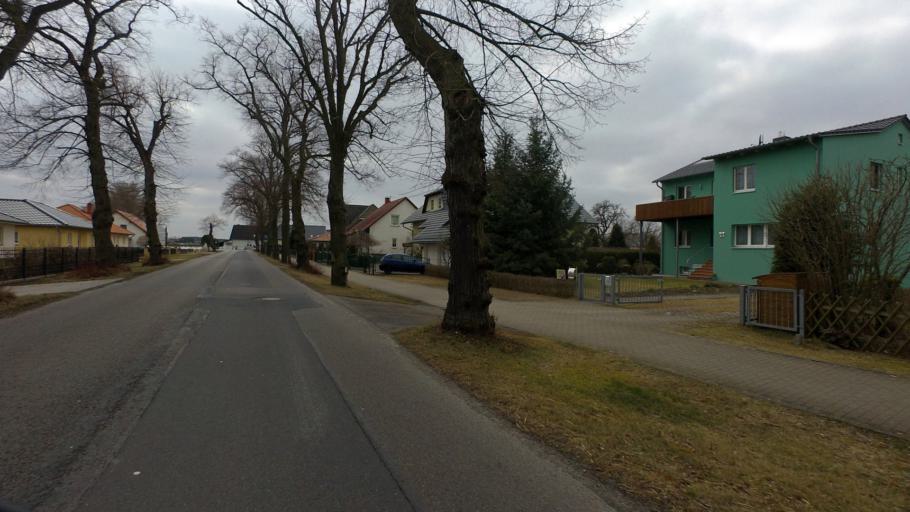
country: DE
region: Brandenburg
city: Trebbin
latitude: 52.2099
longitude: 13.2101
